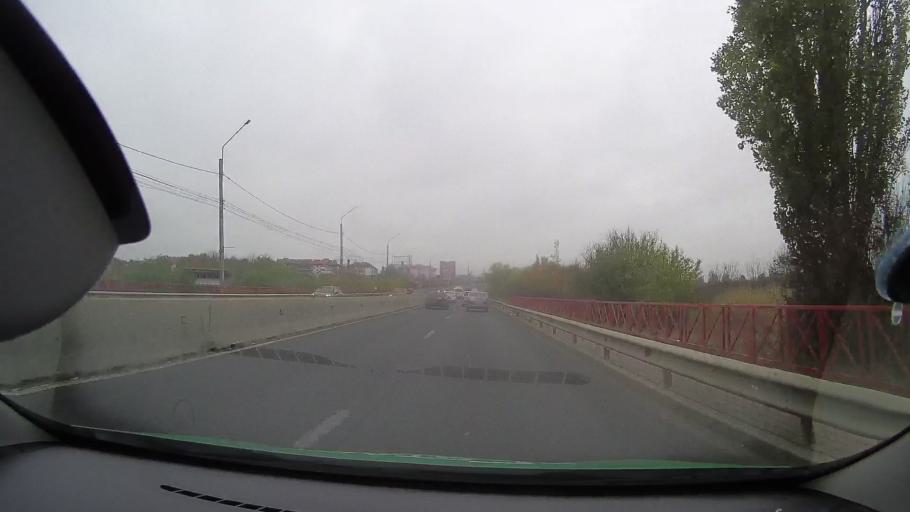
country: RO
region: Ilfov
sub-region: Comuna Corbeanca
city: Corbeanca
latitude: 44.6137
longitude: 26.0708
